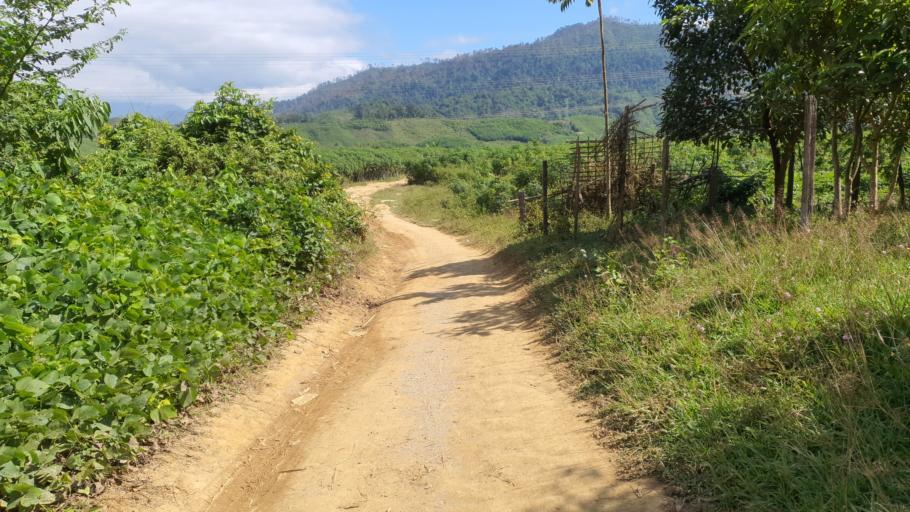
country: LA
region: Bolikhamxai
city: Bolikhan
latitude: 18.9056
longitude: 103.7406
